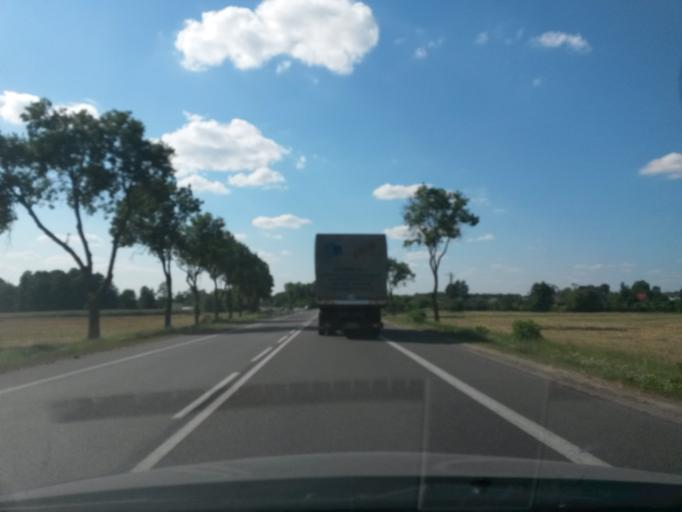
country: PL
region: Masovian Voivodeship
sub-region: Powiat plonski
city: Plonsk
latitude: 52.6178
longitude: 20.3291
